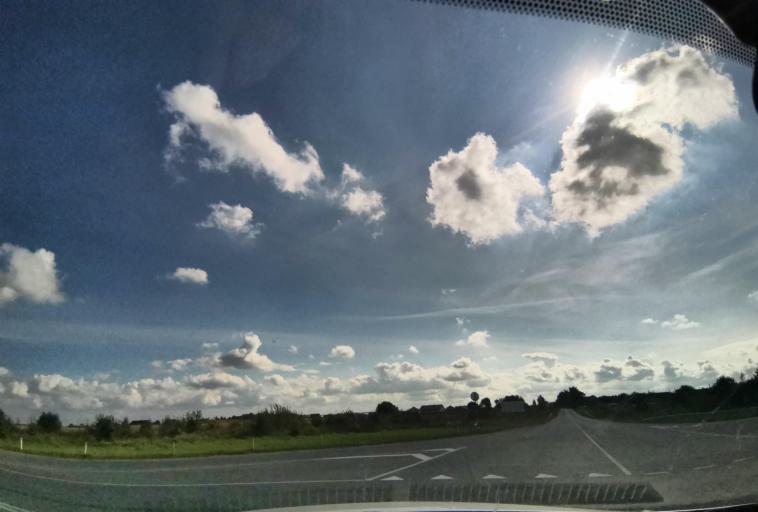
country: RU
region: Kaliningrad
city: Gusev
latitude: 54.6130
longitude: 22.1430
